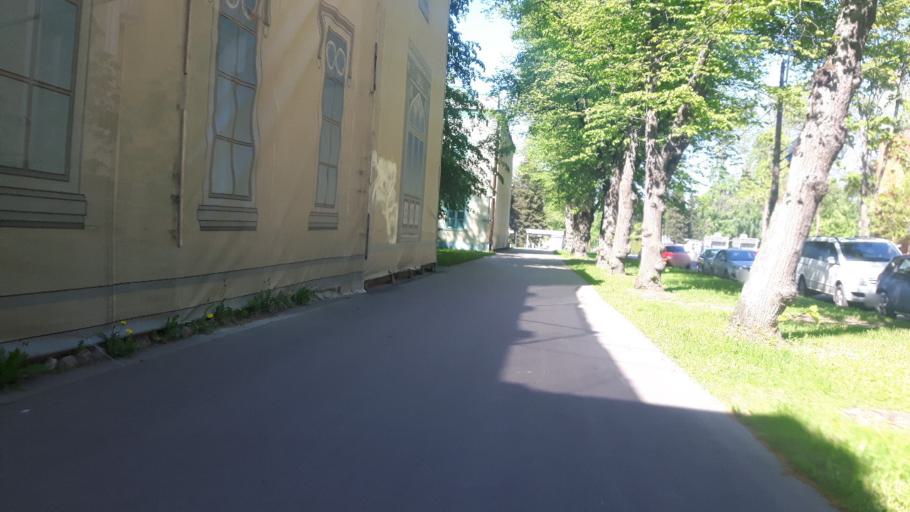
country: RU
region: St.-Petersburg
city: Peterhof
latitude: 59.8799
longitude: 29.9240
